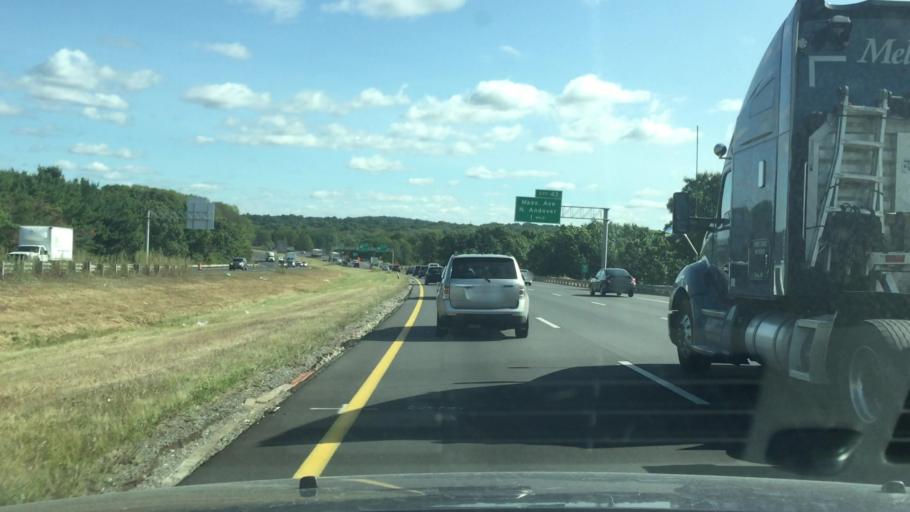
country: US
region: Massachusetts
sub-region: Essex County
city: North Andover
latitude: 42.6809
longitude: -71.1481
